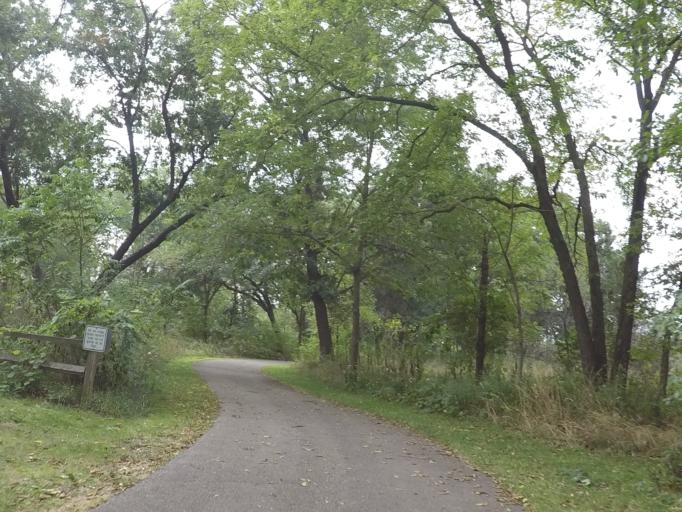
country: US
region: Wisconsin
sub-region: Sauk County
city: Sauk City
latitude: 43.2771
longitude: -89.7182
